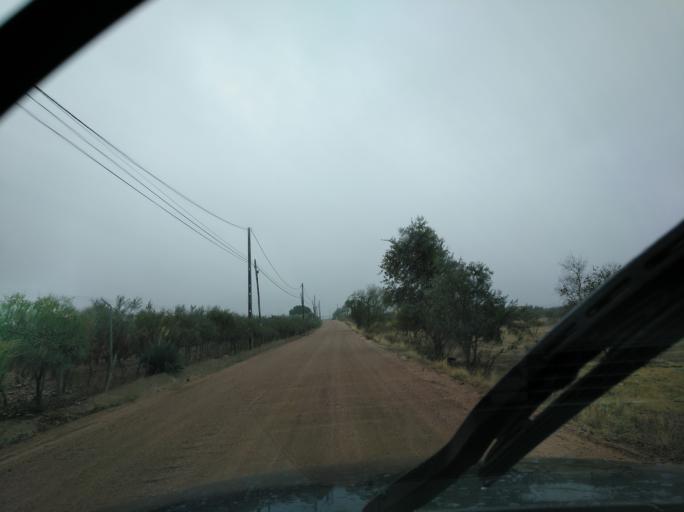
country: PT
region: Portalegre
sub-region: Campo Maior
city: Campo Maior
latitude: 38.9574
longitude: -7.0715
